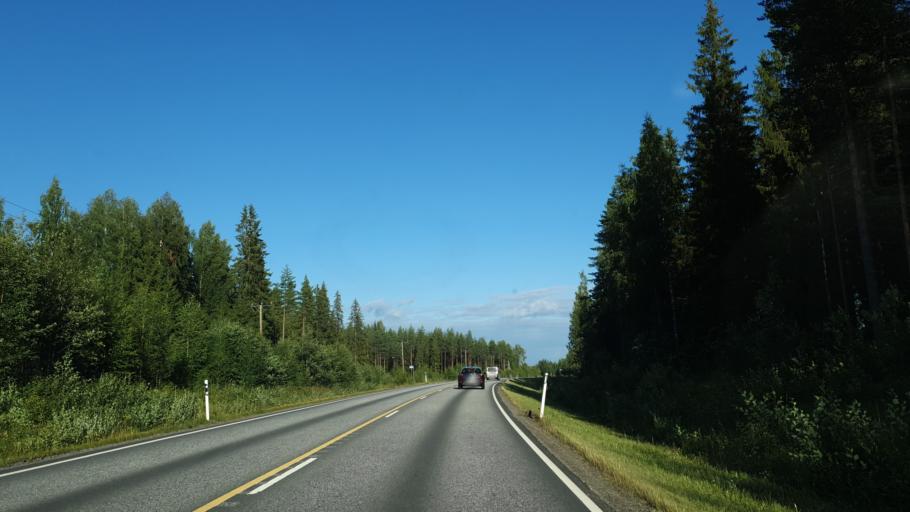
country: FI
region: North Karelia
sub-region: Joensuu
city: Outokumpu
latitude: 62.5348
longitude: 28.9481
